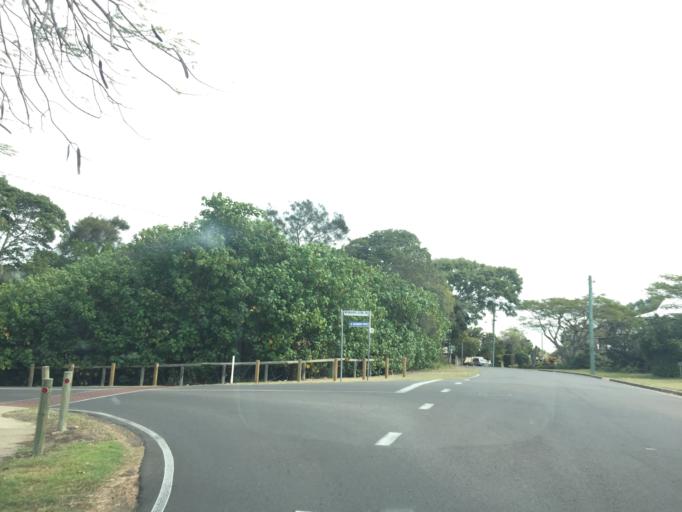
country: AU
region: Queensland
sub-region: Bundaberg
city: Bundaberg
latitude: -24.8295
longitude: 152.4672
